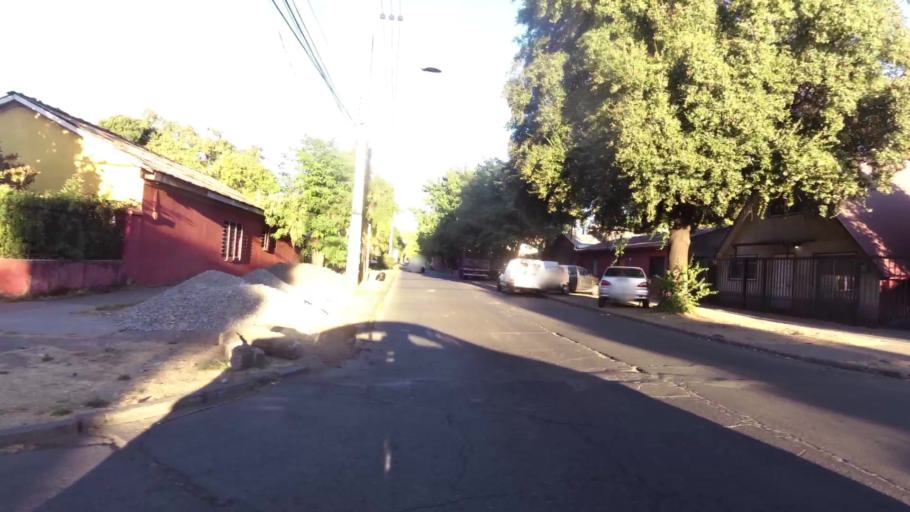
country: CL
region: Maule
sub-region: Provincia de Curico
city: Curico
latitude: -34.9932
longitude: -71.2390
